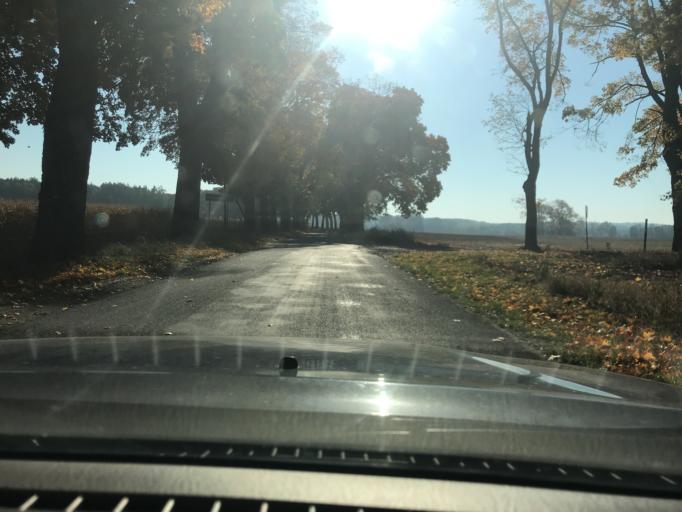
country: PL
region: West Pomeranian Voivodeship
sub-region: Powiat choszczenski
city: Recz
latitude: 53.1637
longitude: 15.6148
